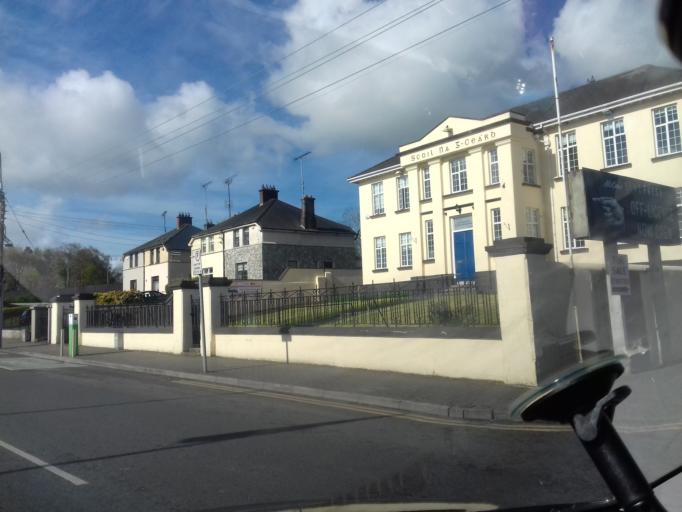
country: IE
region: Leinster
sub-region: An Mhi
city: Kells
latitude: 53.7232
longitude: -6.8809
